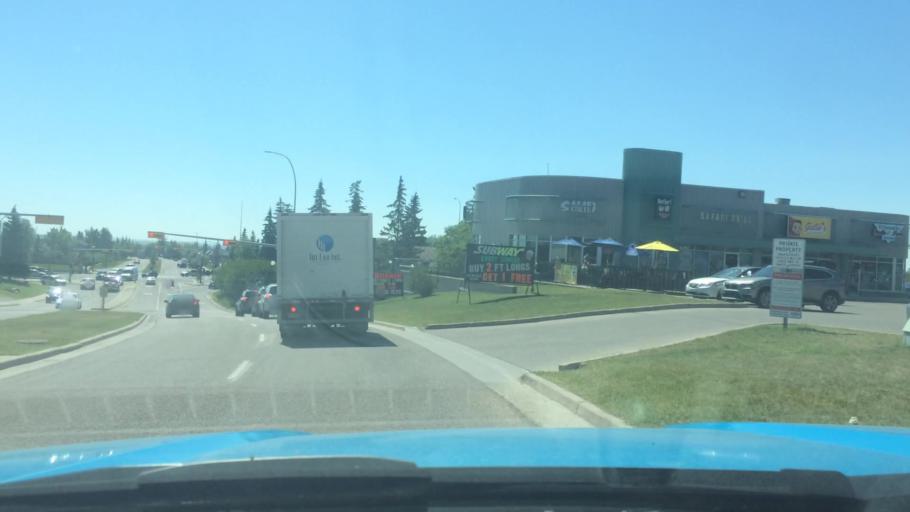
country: CA
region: Alberta
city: Calgary
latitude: 51.0504
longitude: -113.9932
